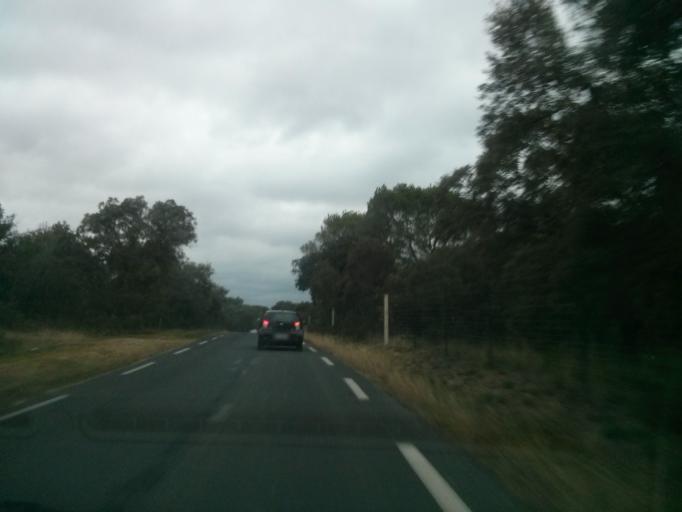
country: FR
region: Languedoc-Roussillon
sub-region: Departement de l'Herault
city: Boisseron
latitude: 43.7596
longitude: 4.1094
